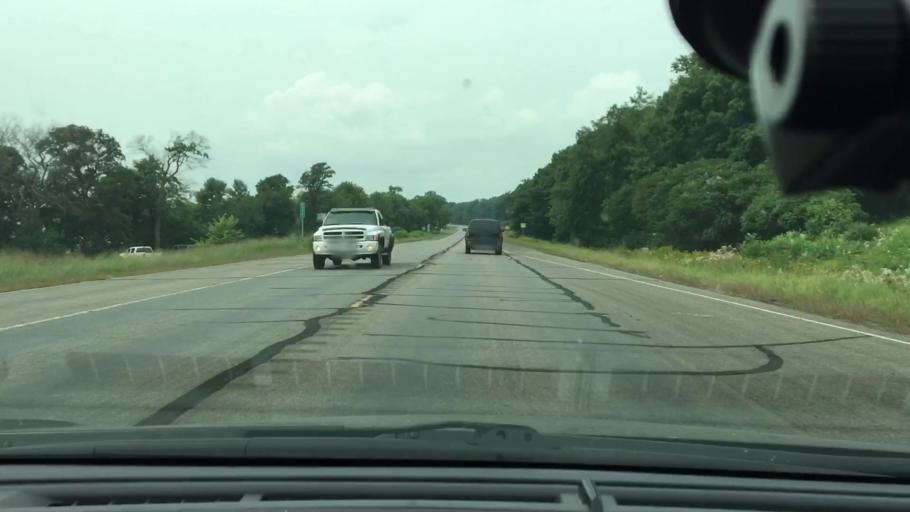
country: US
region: Minnesota
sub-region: Mille Lacs County
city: Vineland
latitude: 46.3271
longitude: -93.7784
